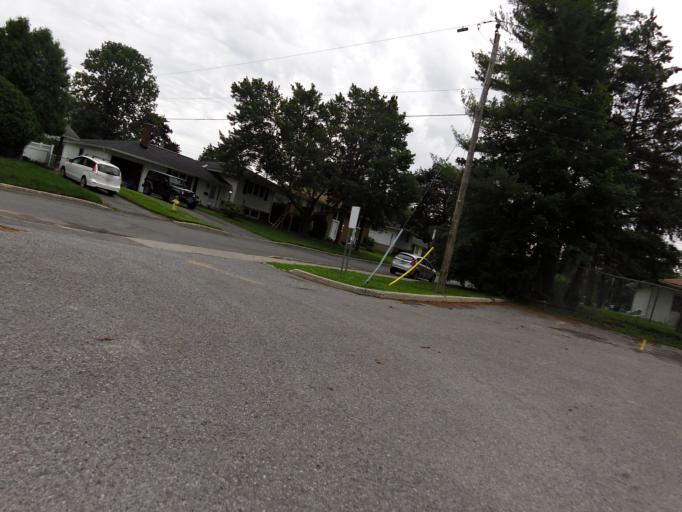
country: CA
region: Ontario
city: Bells Corners
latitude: 45.3368
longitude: -75.7877
